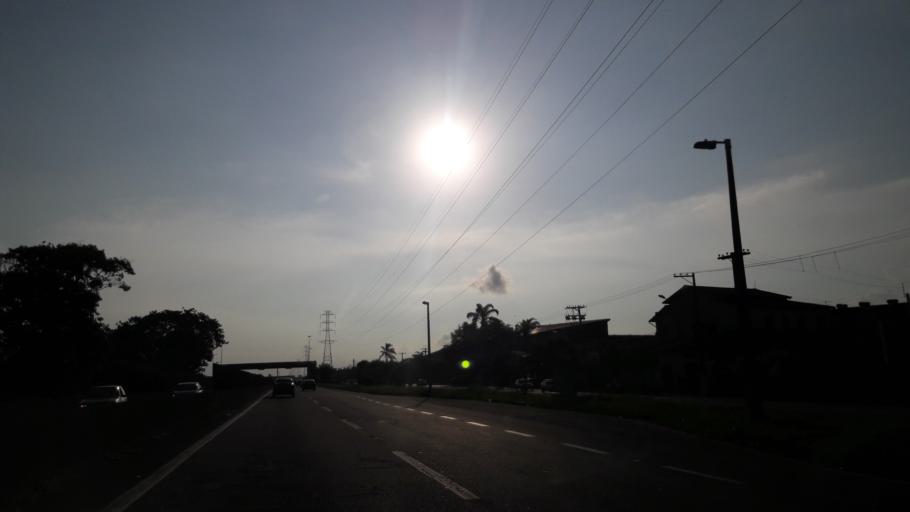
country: BR
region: Sao Paulo
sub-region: Mongagua
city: Mongagua
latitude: -24.1097
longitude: -46.6537
